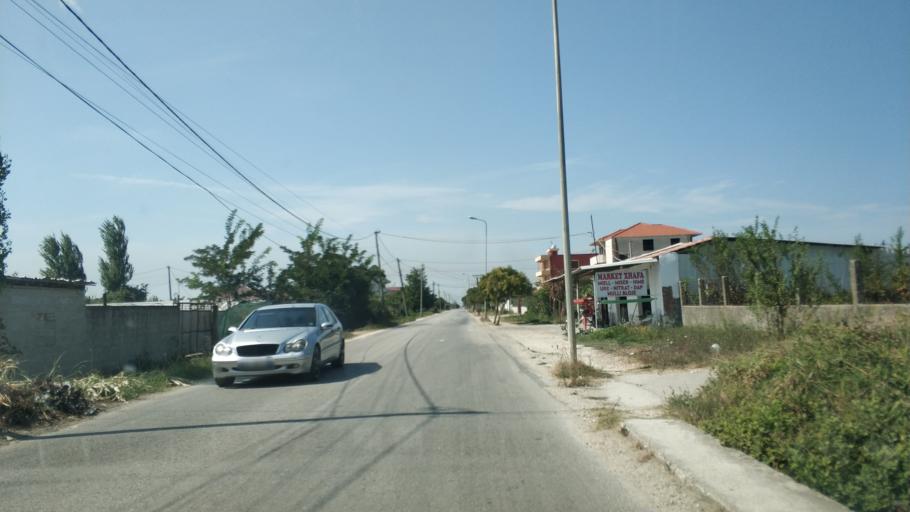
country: AL
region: Fier
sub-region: Rrethi i Fierit
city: Dermenas
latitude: 40.7434
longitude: 19.4996
